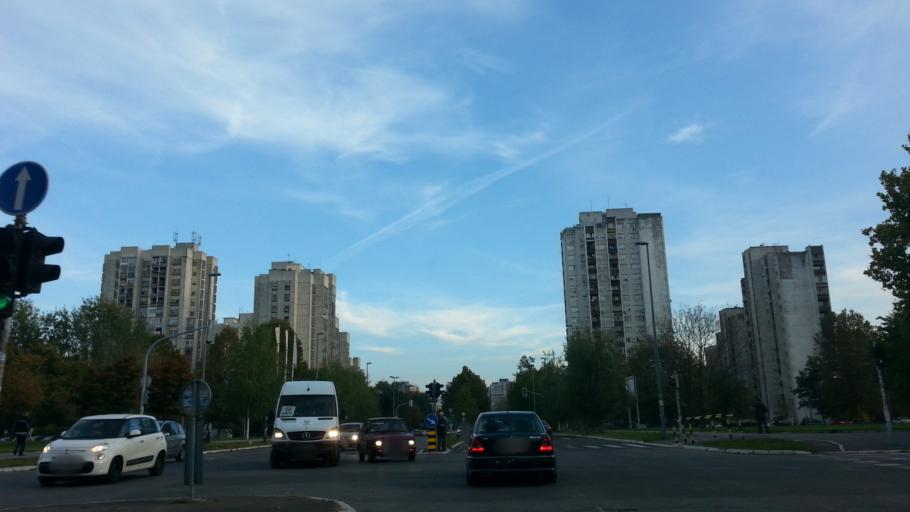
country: RS
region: Central Serbia
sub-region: Belgrade
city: Zemun
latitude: 44.8079
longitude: 20.3846
